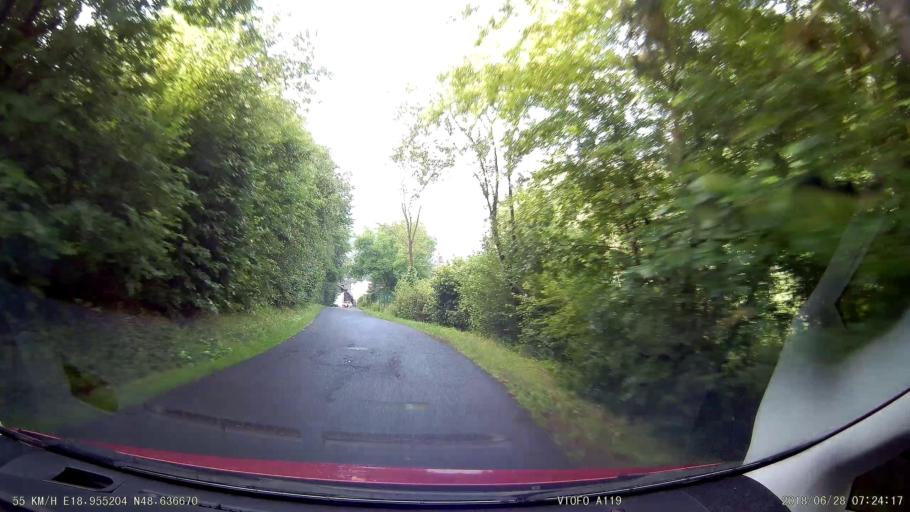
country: SK
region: Banskobystricky
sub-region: Okres Ziar nad Hronom
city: Kremnica
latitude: 48.6365
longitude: 18.9552
